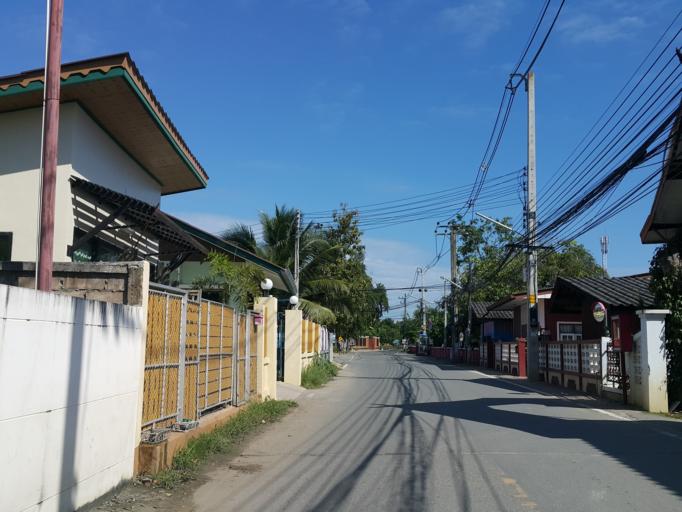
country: TH
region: Chiang Mai
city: San Sai
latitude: 18.7954
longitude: 99.0460
